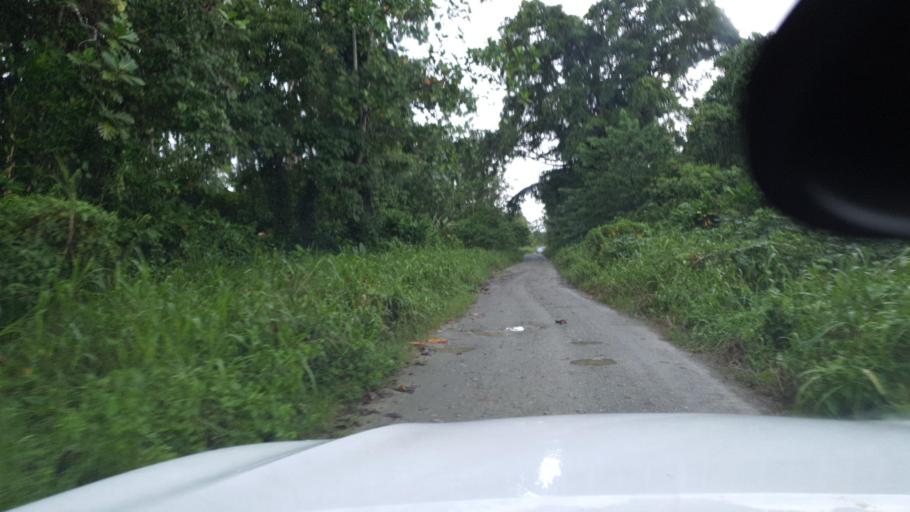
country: SB
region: Guadalcanal
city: Honiara
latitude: -9.4645
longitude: 160.3647
